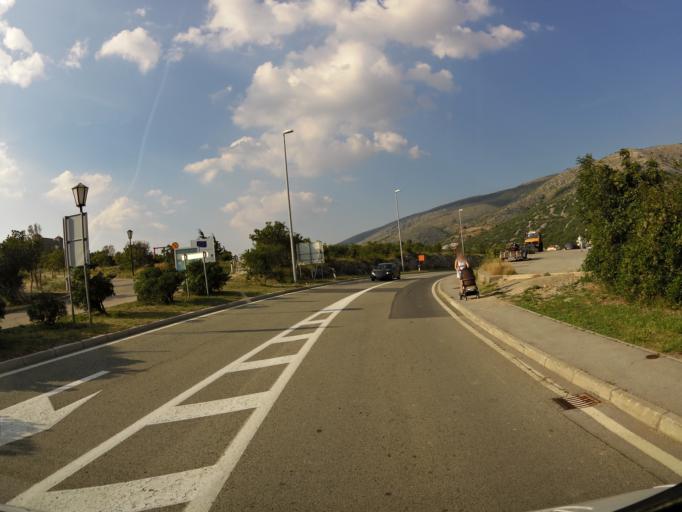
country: HR
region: Licko-Senjska
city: Senj
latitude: 44.9846
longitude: 14.9060
